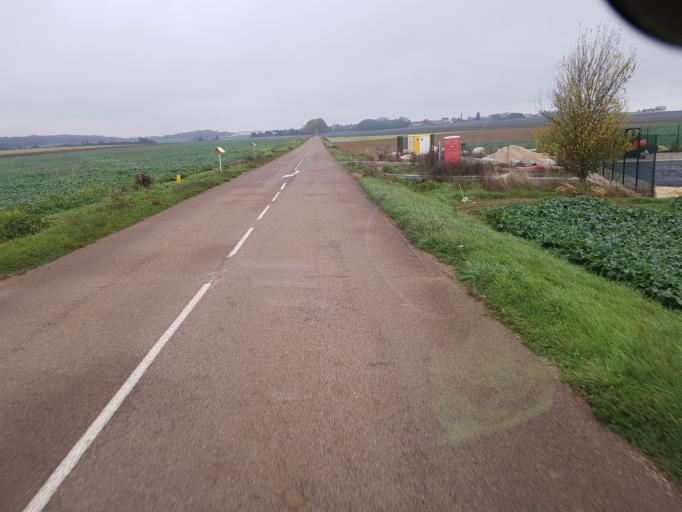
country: FR
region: Bourgogne
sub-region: Departement de la Cote-d'Or
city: Saint-Julien
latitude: 47.4312
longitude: 5.2130
